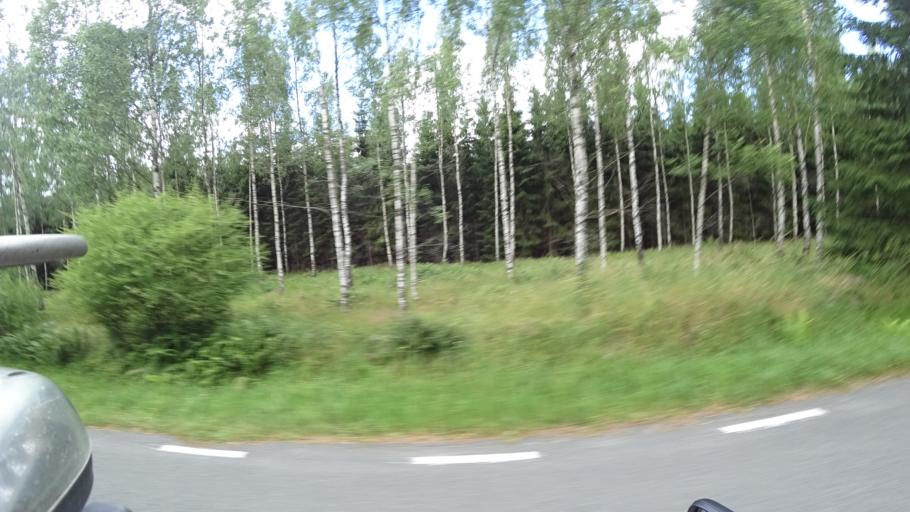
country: SE
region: Skane
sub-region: Kristianstads Kommun
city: Degeberga
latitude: 55.7657
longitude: 13.9810
